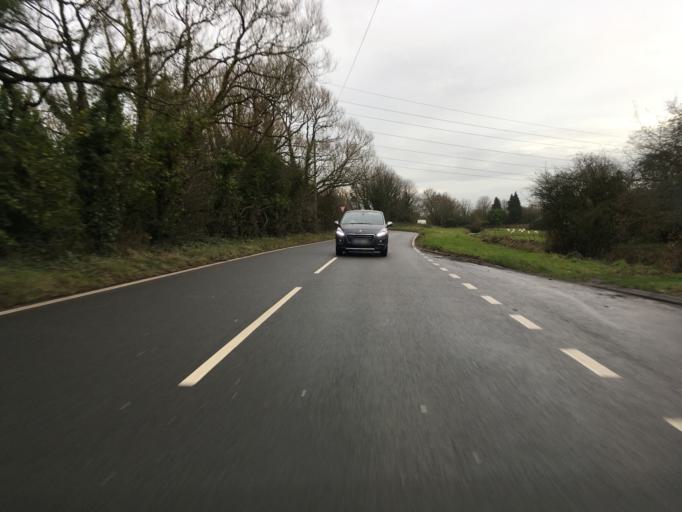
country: GB
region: Wales
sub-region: Newport
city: Nash
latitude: 51.5637
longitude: -2.9483
